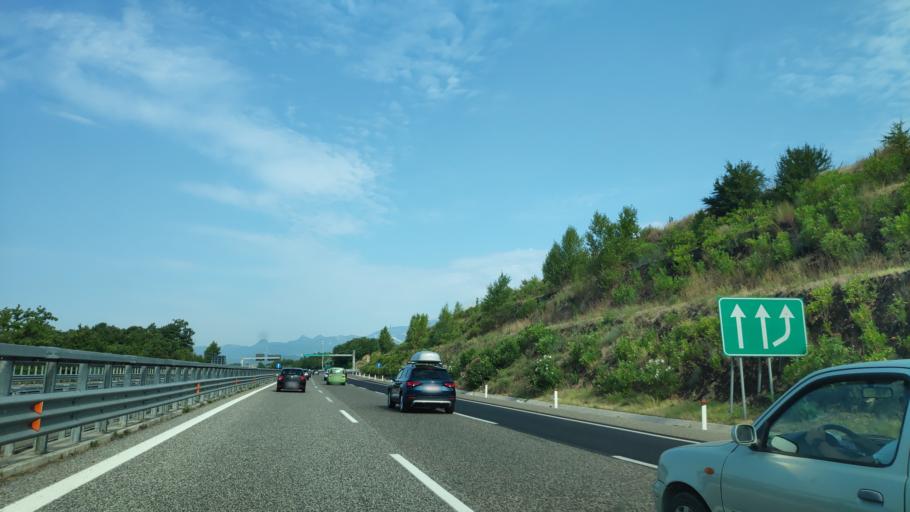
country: IT
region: Campania
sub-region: Provincia di Salerno
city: Palomonte
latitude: 40.6115
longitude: 15.2839
